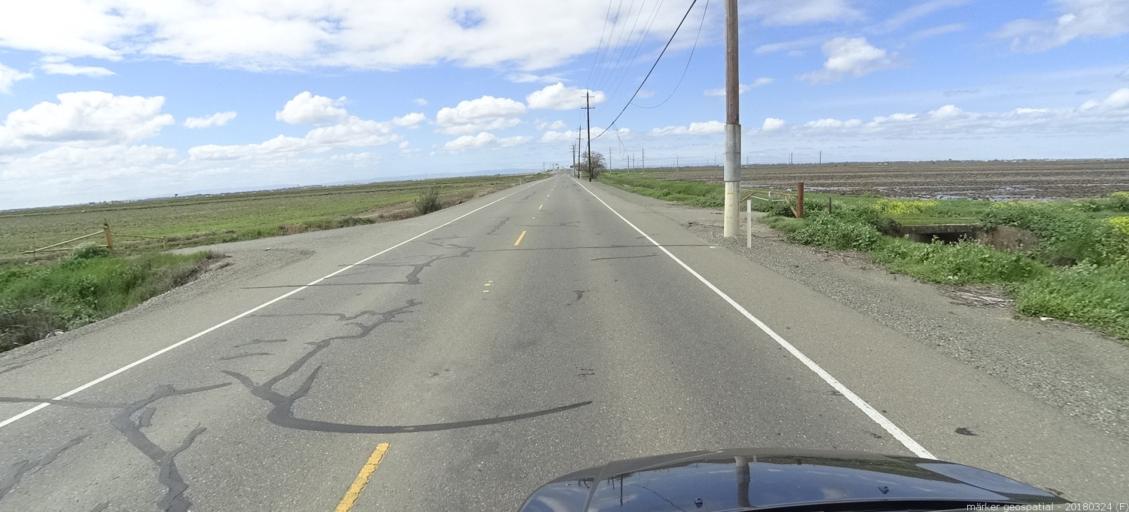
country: US
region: California
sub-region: Sacramento County
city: Elverta
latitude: 38.7143
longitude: -121.5304
